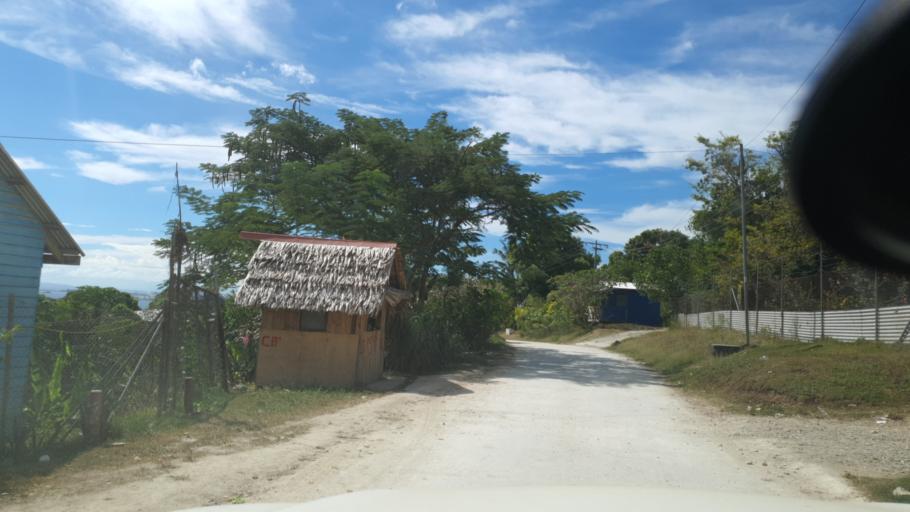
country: SB
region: Guadalcanal
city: Honiara
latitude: -9.4378
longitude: 159.9788
